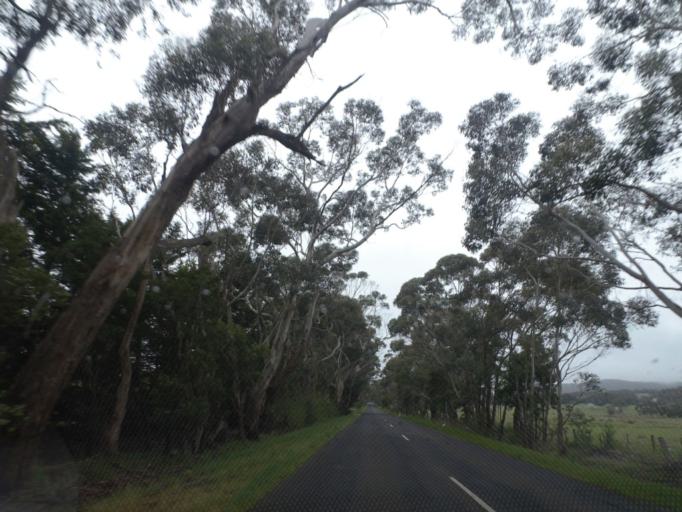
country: AU
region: Victoria
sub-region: Hume
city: Sunbury
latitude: -37.3444
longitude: 144.5937
